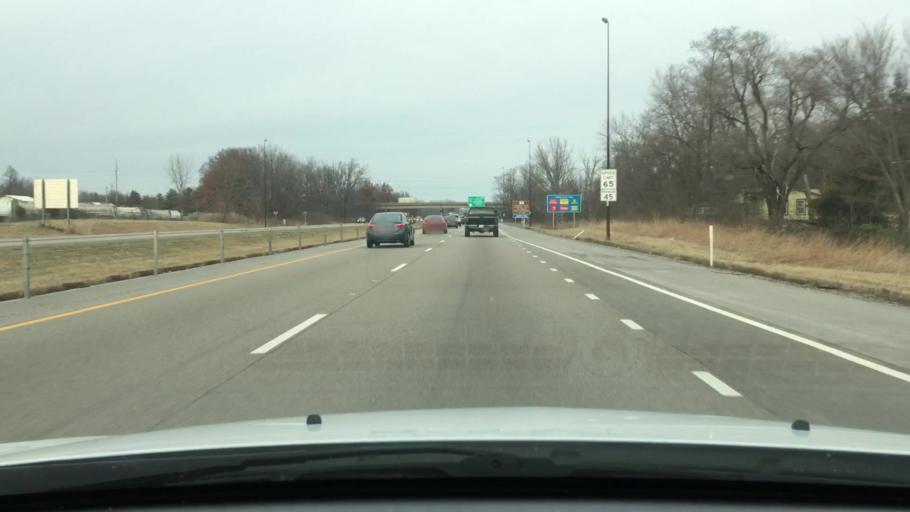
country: US
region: Illinois
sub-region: Sangamon County
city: Grandview
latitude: 39.7917
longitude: -89.5978
